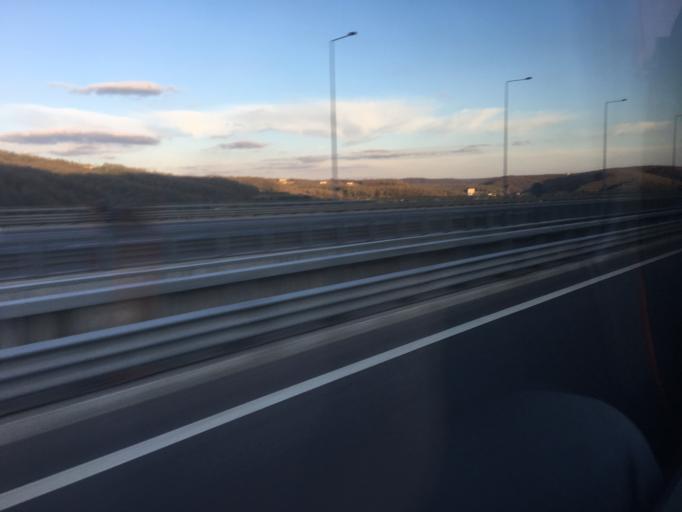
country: TR
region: Istanbul
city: Mahmut Sevket Pasa
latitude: 41.1420
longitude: 29.2831
